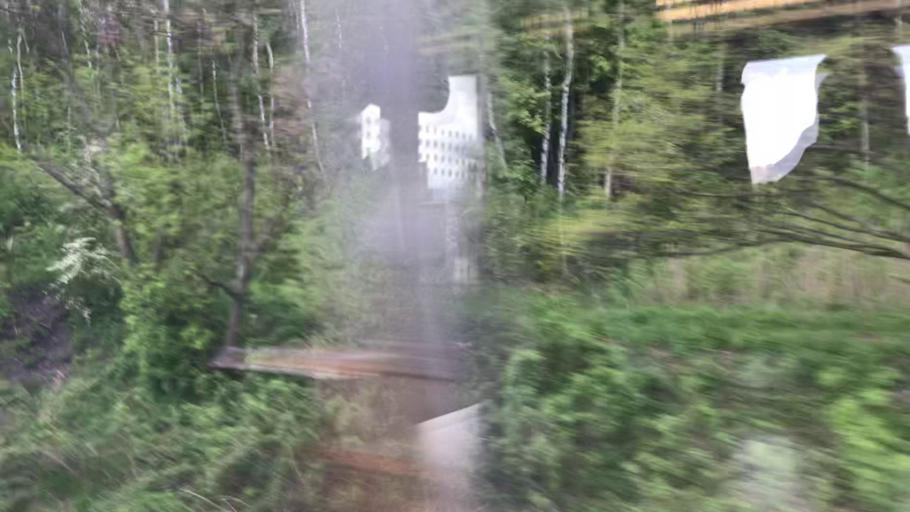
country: PL
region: Lower Silesian Voivodeship
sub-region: Powiat walbrzyski
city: Walbrzych
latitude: 50.7756
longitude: 16.2710
